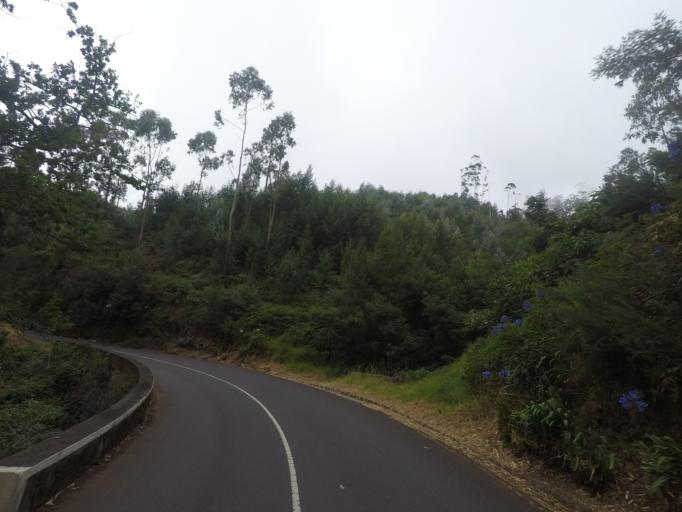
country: PT
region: Madeira
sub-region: Funchal
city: Nossa Senhora do Monte
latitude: 32.6700
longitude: -16.8781
